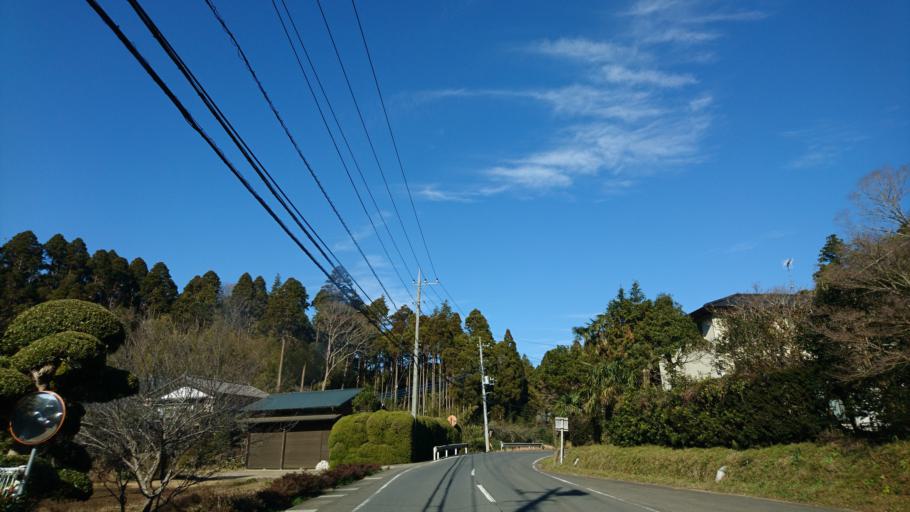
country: JP
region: Chiba
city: Yachimata
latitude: 35.6124
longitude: 140.3456
